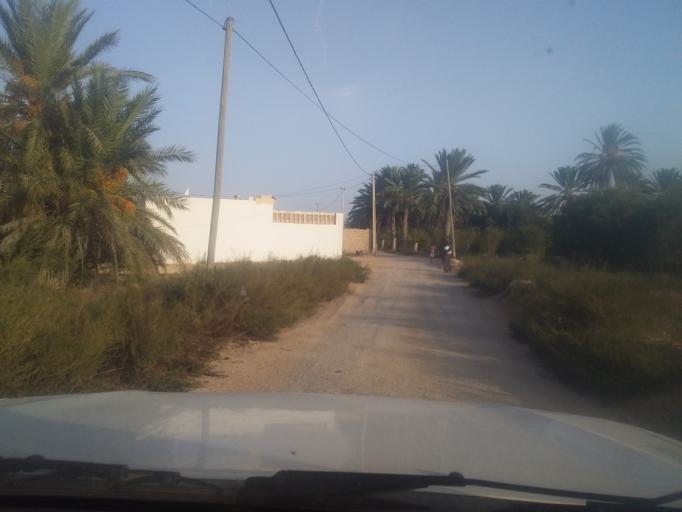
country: TN
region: Qabis
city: Gabes
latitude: 33.6304
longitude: 10.2869
